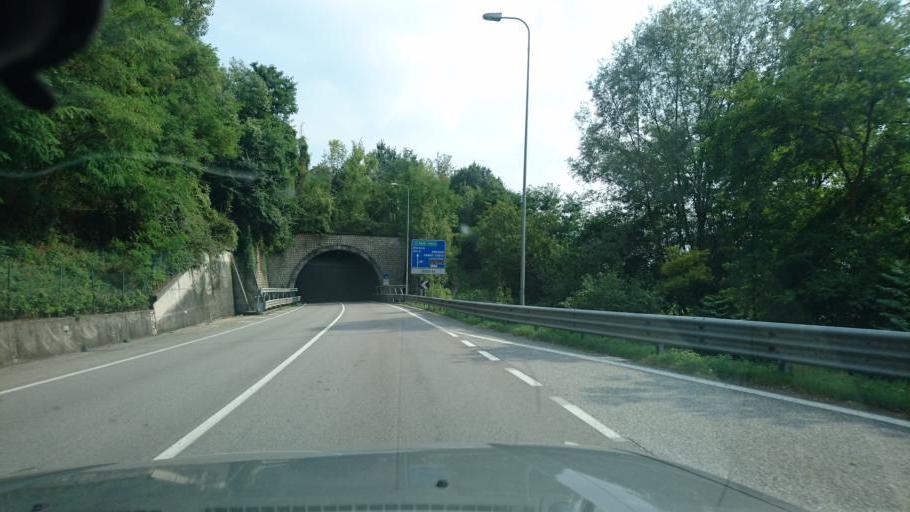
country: IT
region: Lombardy
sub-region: Provincia di Brescia
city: Barghe
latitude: 45.6668
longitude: 10.4124
